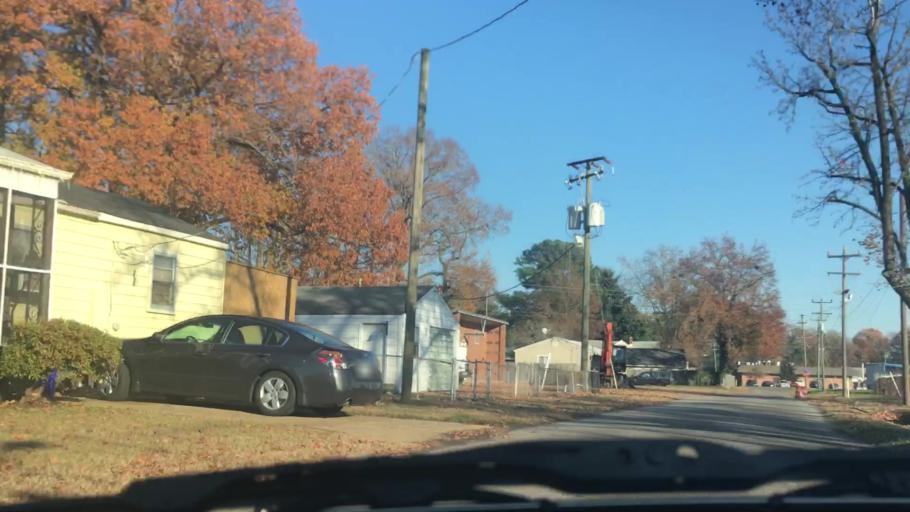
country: US
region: Virginia
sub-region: City of Norfolk
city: Norfolk
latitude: 36.9166
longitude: -76.2438
